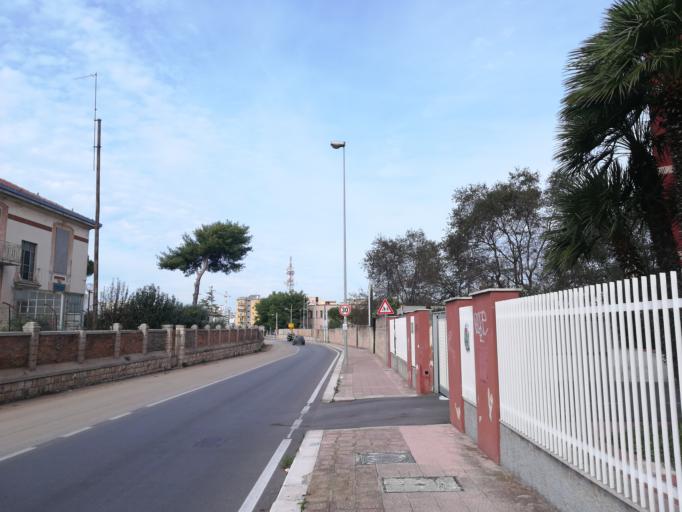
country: IT
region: Apulia
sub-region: Provincia di Bari
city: Bari
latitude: 41.1116
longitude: 16.8890
